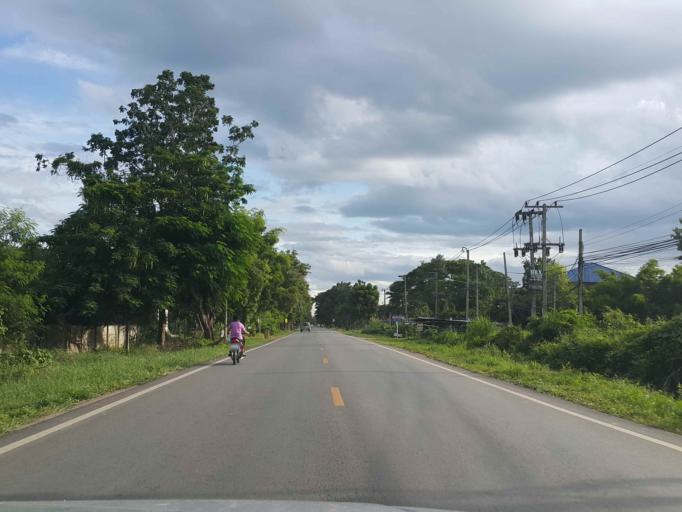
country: TH
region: Sukhothai
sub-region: Amphoe Si Satchanalai
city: Si Satchanalai
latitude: 17.5144
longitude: 99.7557
